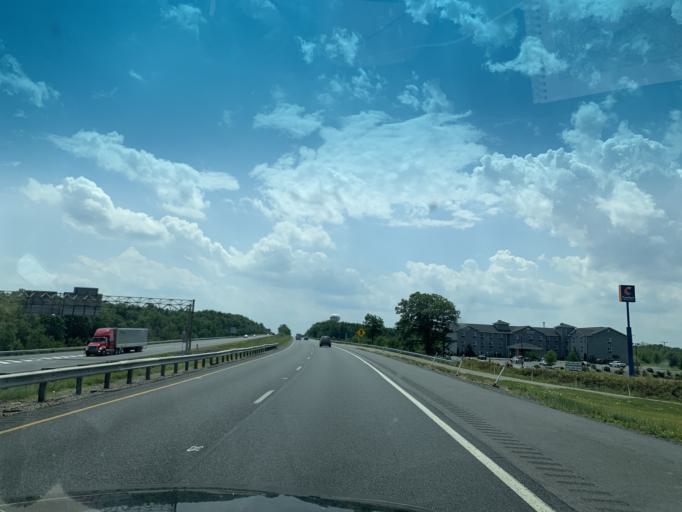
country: US
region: Pennsylvania
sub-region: Schuylkill County
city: Mahanoy City
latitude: 40.8095
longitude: -76.1067
